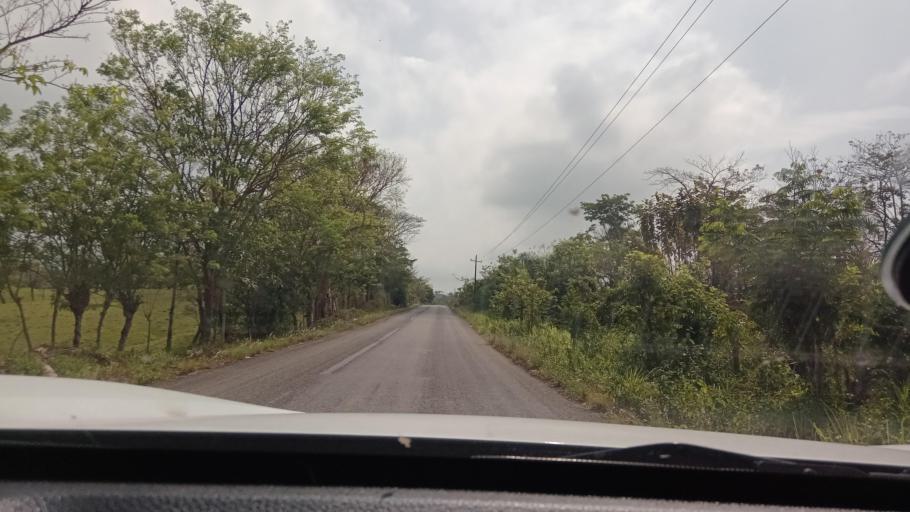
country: MX
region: Tabasco
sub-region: Huimanguillo
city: Francisco Rueda
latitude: 17.5739
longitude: -94.1068
